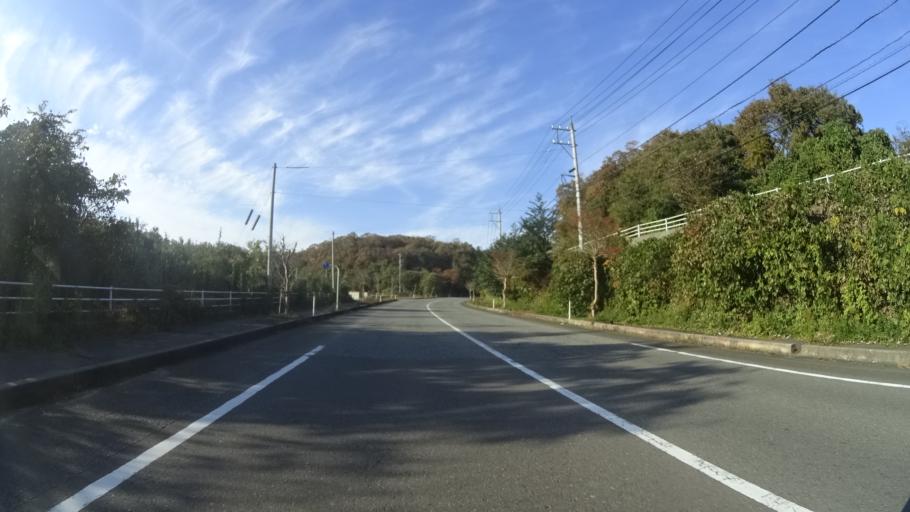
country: JP
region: Ishikawa
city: Hakui
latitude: 37.0332
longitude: 136.7795
